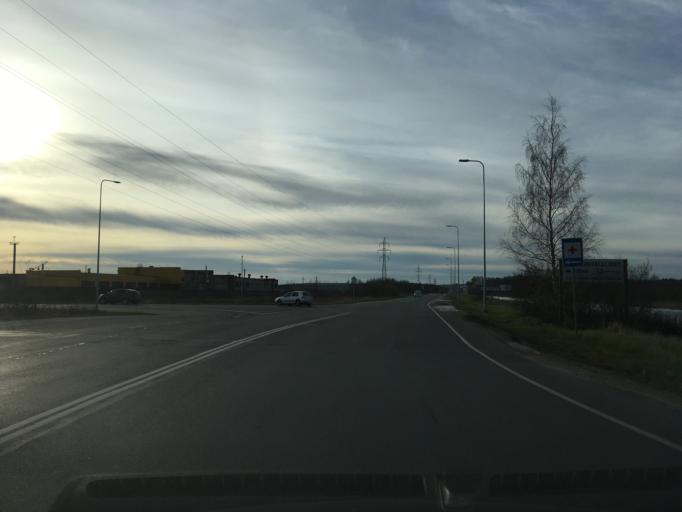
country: EE
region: Ida-Virumaa
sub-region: Narva linn
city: Narva
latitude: 59.3697
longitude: 28.1553
